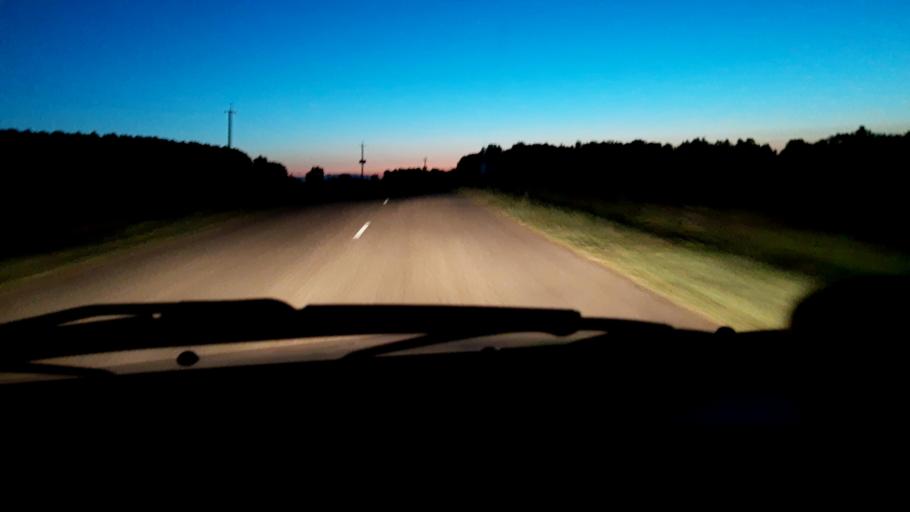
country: RU
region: Bashkortostan
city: Blagoveshchensk
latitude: 54.9378
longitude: 55.8919
